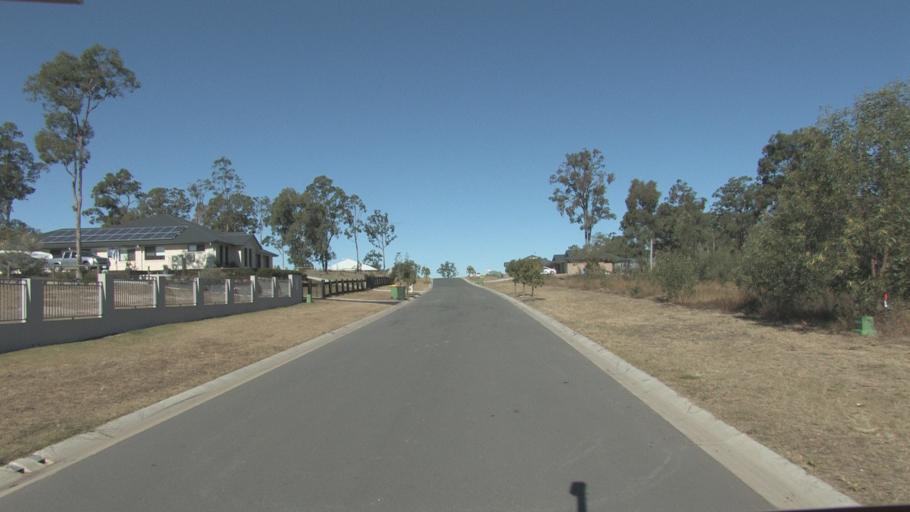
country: AU
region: Queensland
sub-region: Logan
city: North Maclean
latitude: -27.7540
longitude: 152.9433
